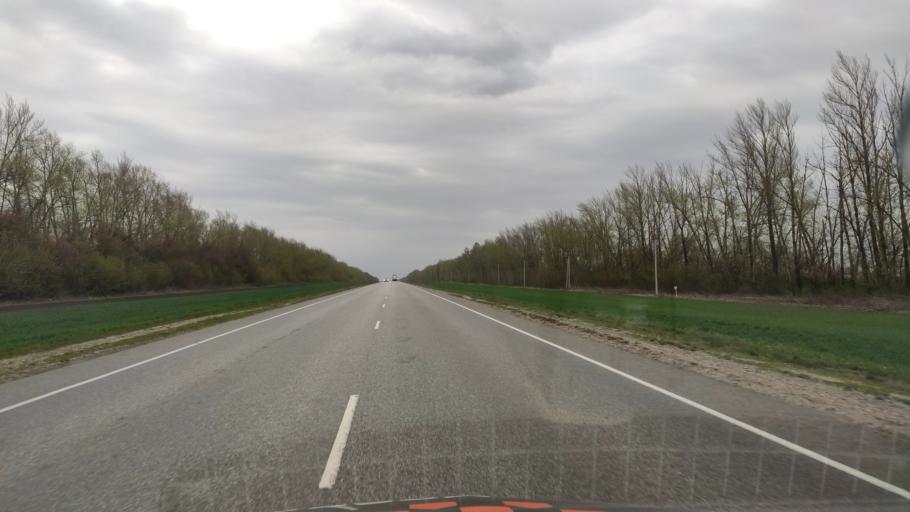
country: RU
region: Kursk
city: Gorshechnoye
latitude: 51.5496
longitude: 38.1645
